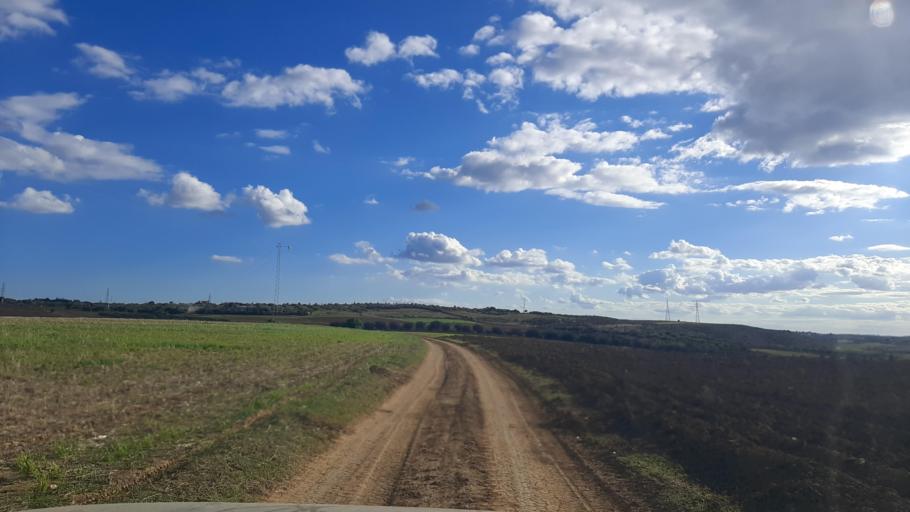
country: TN
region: Nabul
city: Bu `Urqub
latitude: 36.4481
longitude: 10.5013
